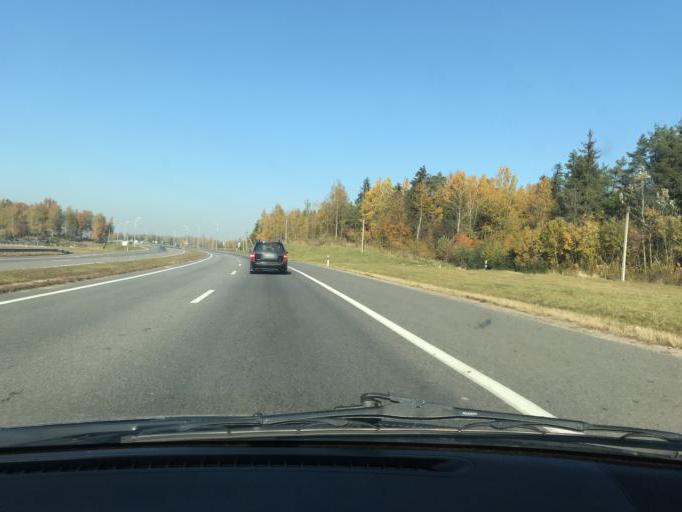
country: BY
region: Minsk
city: Samakhvalavichy
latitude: 53.7007
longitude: 27.5265
